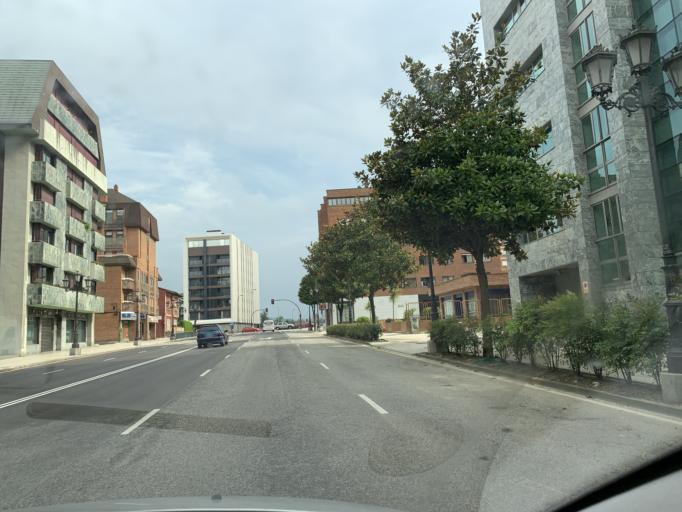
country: ES
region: Asturias
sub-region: Province of Asturias
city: Oviedo
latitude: 43.3577
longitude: -5.8574
